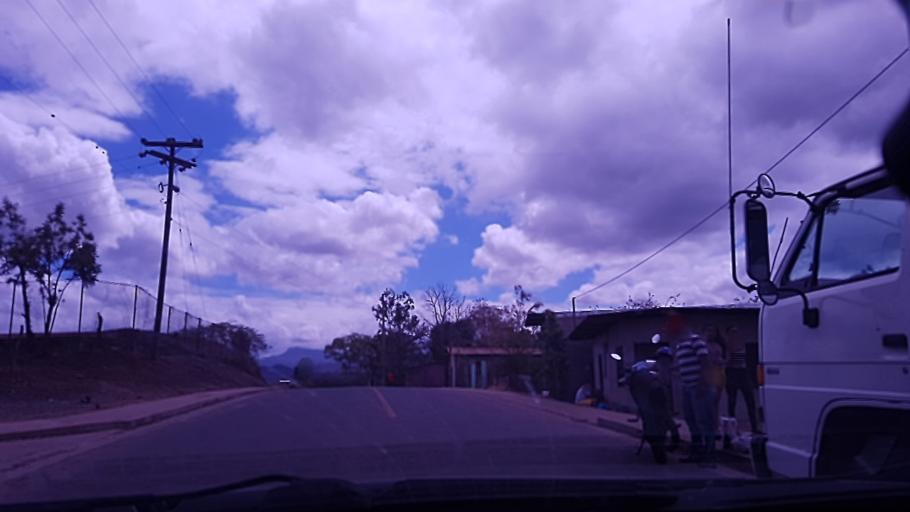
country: NI
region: Esteli
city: Condega
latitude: 13.3723
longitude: -86.3975
